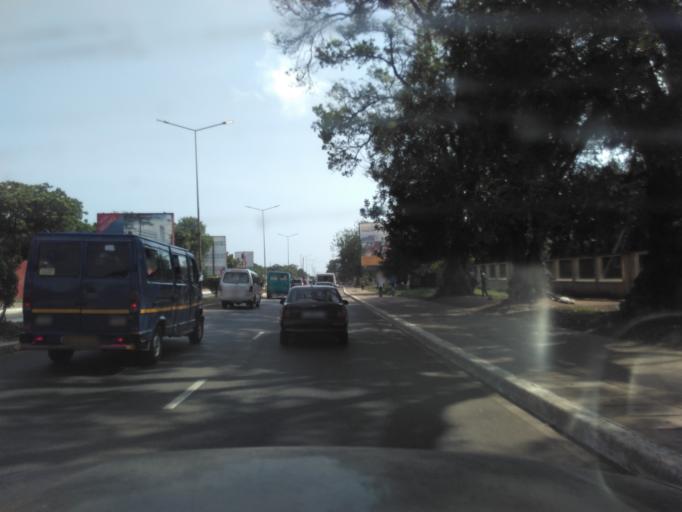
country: GH
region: Greater Accra
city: Accra
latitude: 5.5847
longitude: -0.1846
